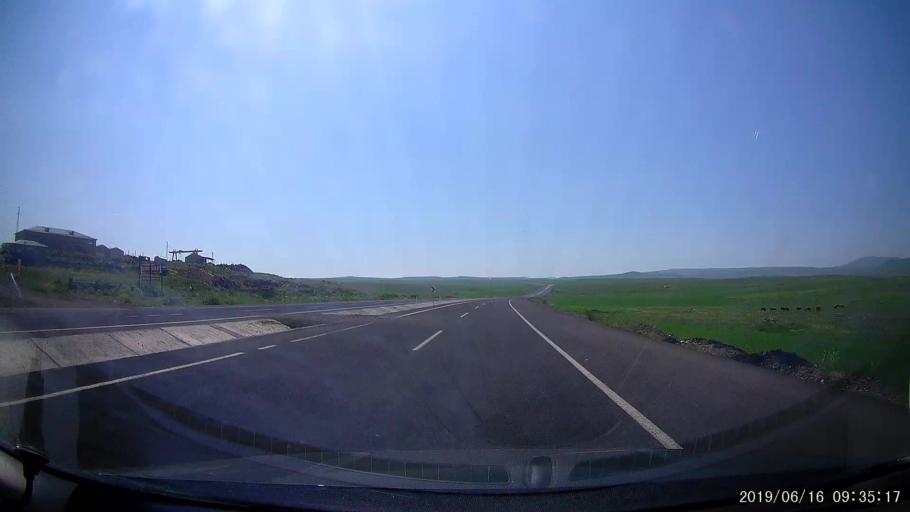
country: TR
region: Kars
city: Kars
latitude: 40.5742
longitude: 43.1533
